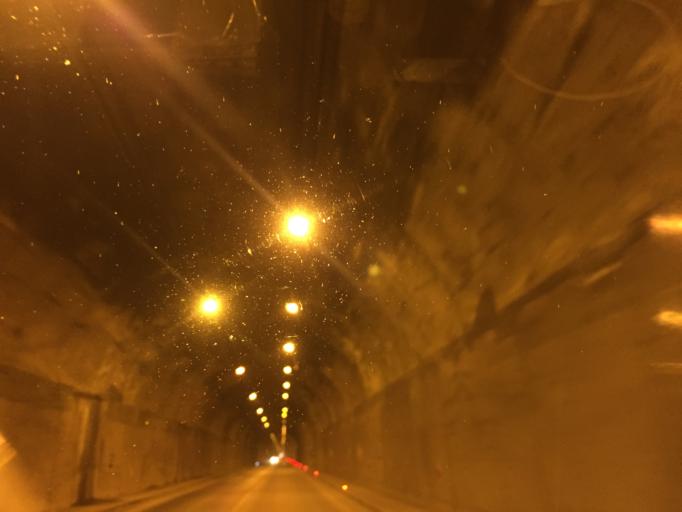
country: TR
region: Gumushane
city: Torul
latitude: 40.6555
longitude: 39.3995
